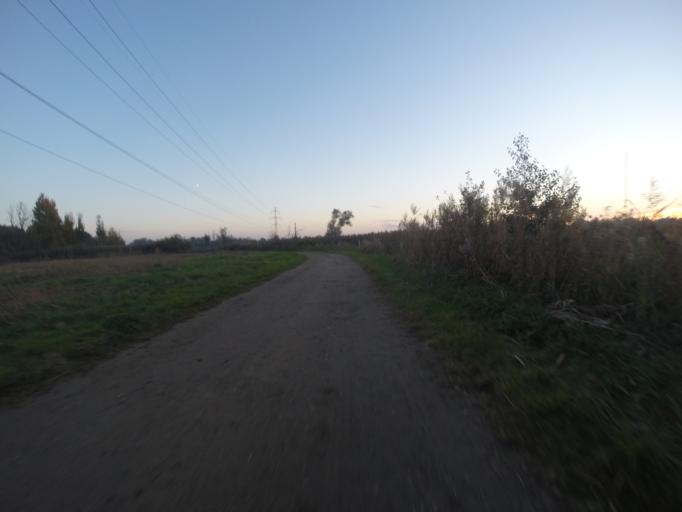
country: DK
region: Capital Region
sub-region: Hoje-Taastrup Kommune
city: Taastrup
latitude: 55.6663
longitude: 12.3195
